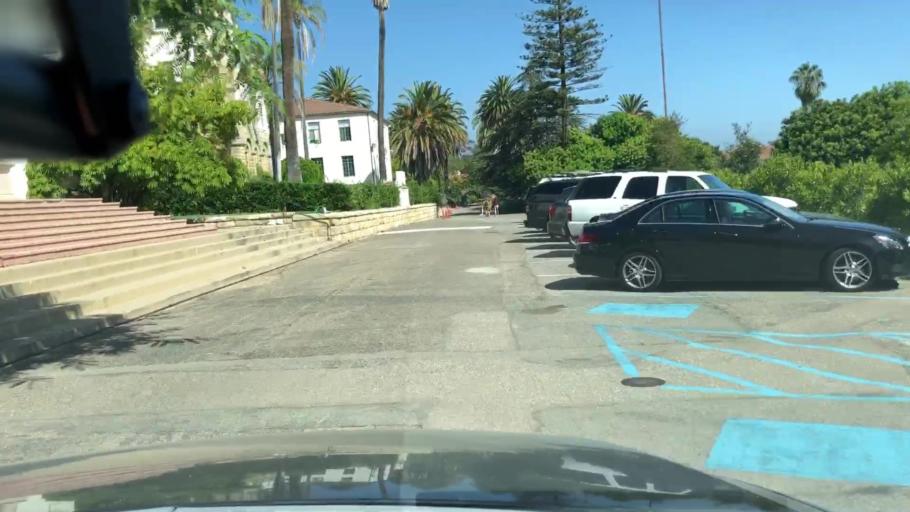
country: US
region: California
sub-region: Santa Barbara County
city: Mission Canyon
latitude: 34.4390
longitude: -119.7165
